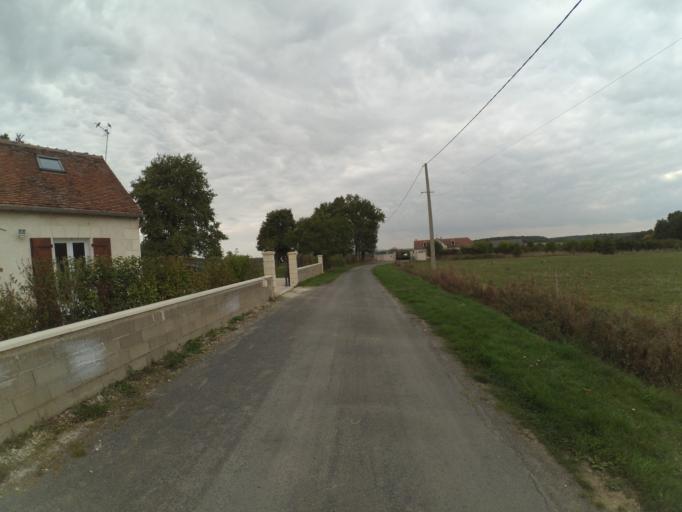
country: FR
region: Centre
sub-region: Departement d'Indre-et-Loire
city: Auzouer-en-Touraine
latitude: 47.4984
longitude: 0.9328
